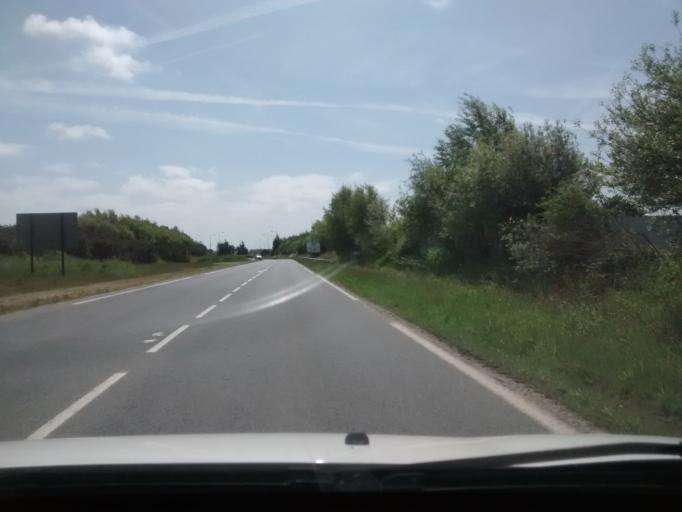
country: FR
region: Brittany
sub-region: Departement des Cotes-d'Armor
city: Lannion
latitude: 48.7545
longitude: -3.4485
